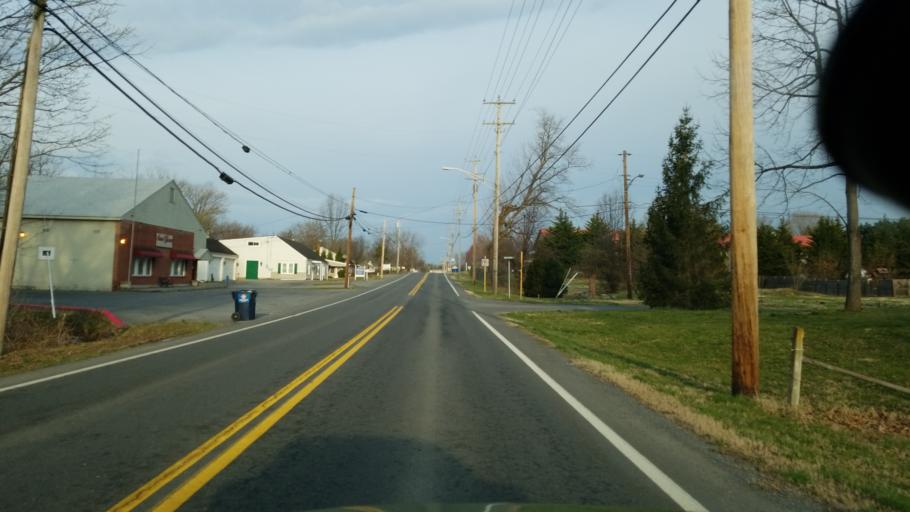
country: US
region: Virginia
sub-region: Clarke County
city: Berryville
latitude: 39.1465
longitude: -77.9682
